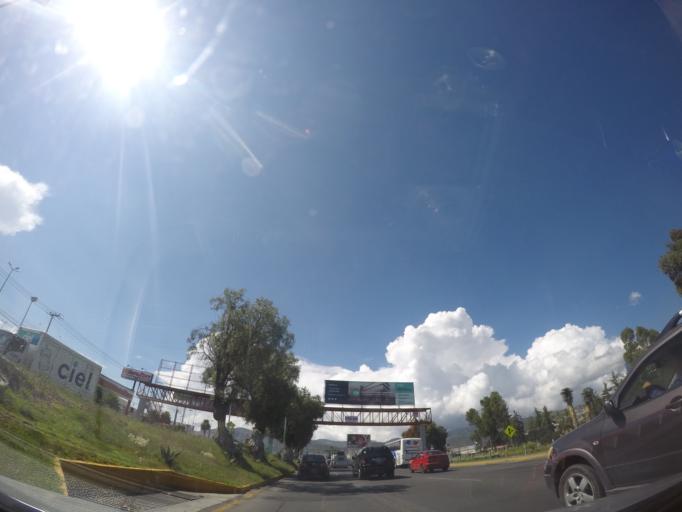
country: MX
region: Hidalgo
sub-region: Mineral de la Reforma
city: Campestre Villas del Alamo
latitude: 20.0961
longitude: -98.7152
